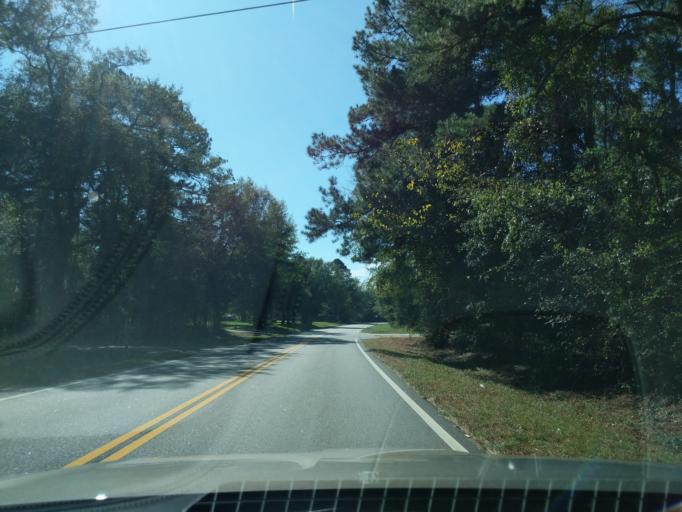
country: US
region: Georgia
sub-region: Richmond County
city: Hephzibah
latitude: 33.3090
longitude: -82.0182
